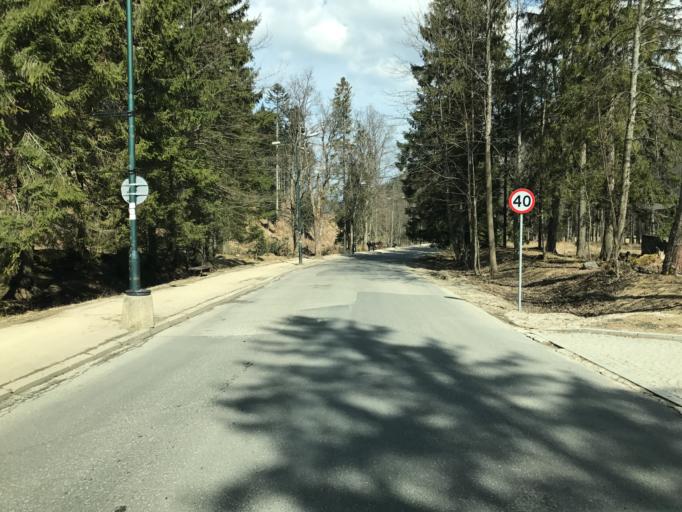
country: PL
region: Lesser Poland Voivodeship
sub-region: Powiat tatrzanski
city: Zakopane
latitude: 49.2708
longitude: 19.9799
